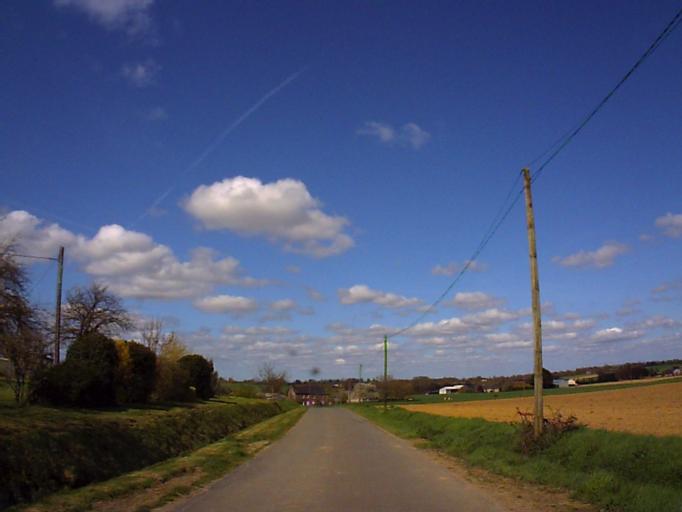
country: FR
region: Brittany
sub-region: Departement d'Ille-et-Vilaine
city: Boisgervilly
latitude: 48.1003
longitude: -2.1141
